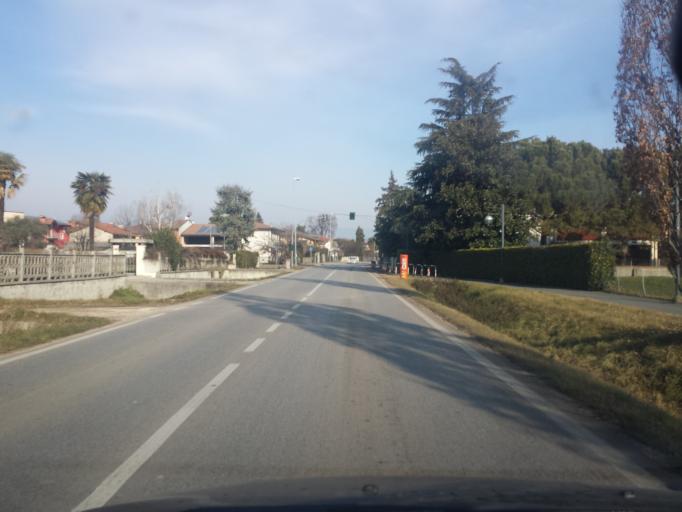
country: IT
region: Veneto
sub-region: Provincia di Vicenza
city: Bressanvido
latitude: 45.6406
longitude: 11.6284
